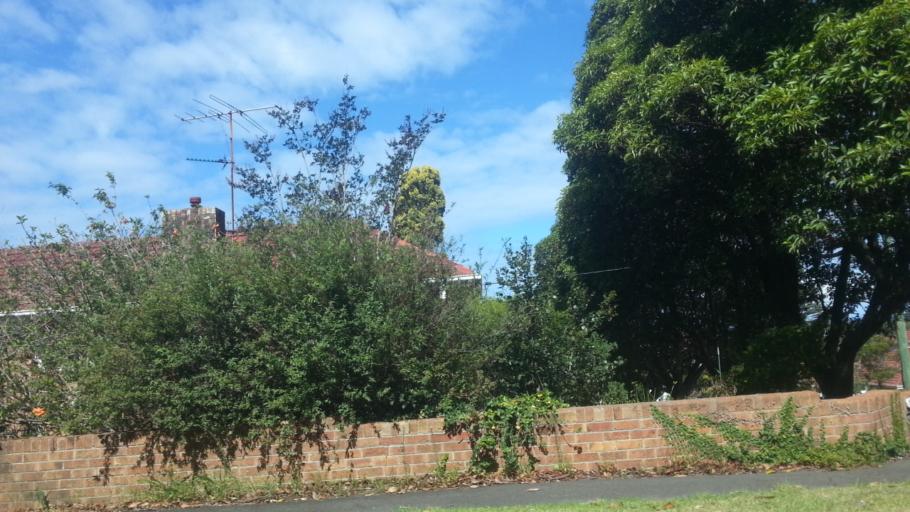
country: AU
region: New South Wales
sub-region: Wollongong
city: Fairy Meadow
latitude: -34.4003
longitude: 150.8865
